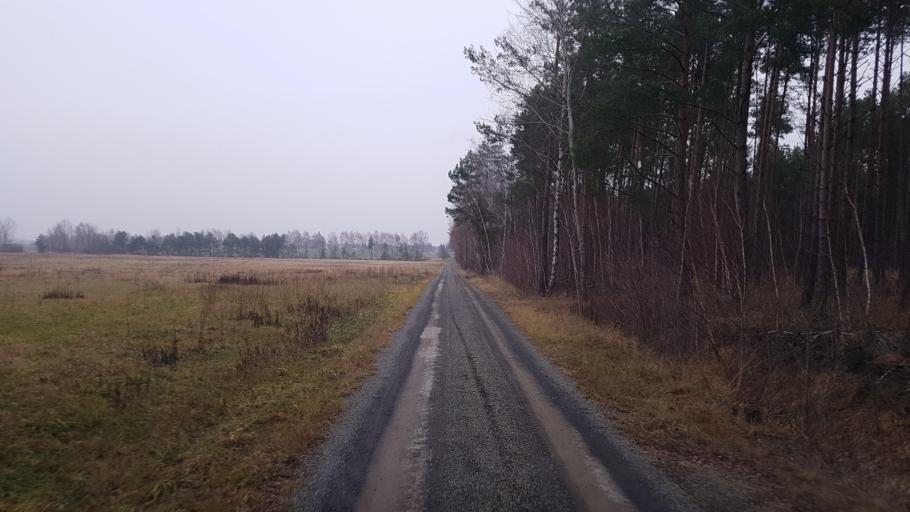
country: DE
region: Brandenburg
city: Plessa
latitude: 51.5237
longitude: 13.6279
